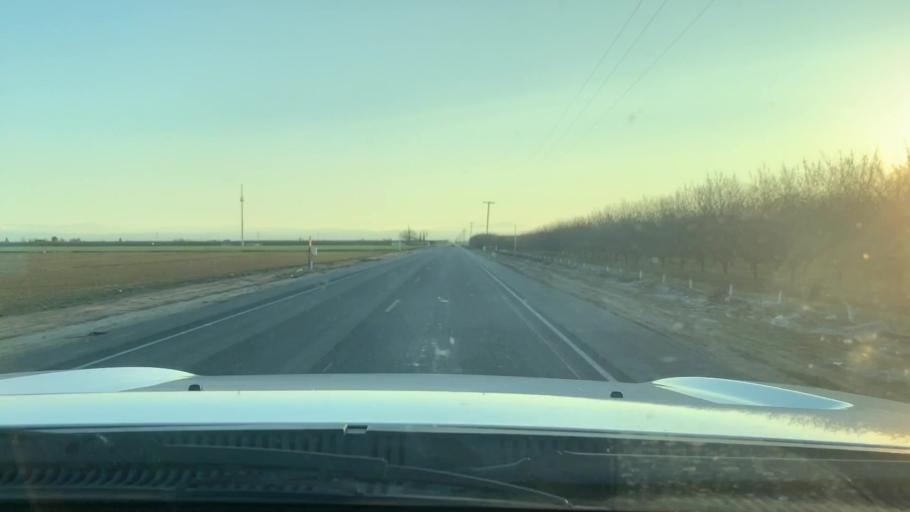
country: US
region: California
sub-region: Kern County
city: Wasco
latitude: 35.5001
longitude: -119.3746
